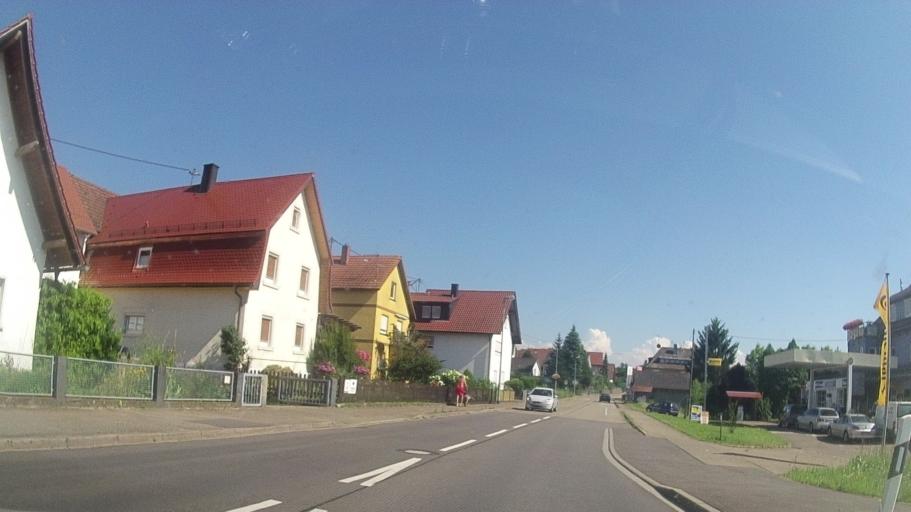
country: DE
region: Baden-Wuerttemberg
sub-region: Freiburg Region
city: Offenburg
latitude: 48.4984
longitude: 7.9302
